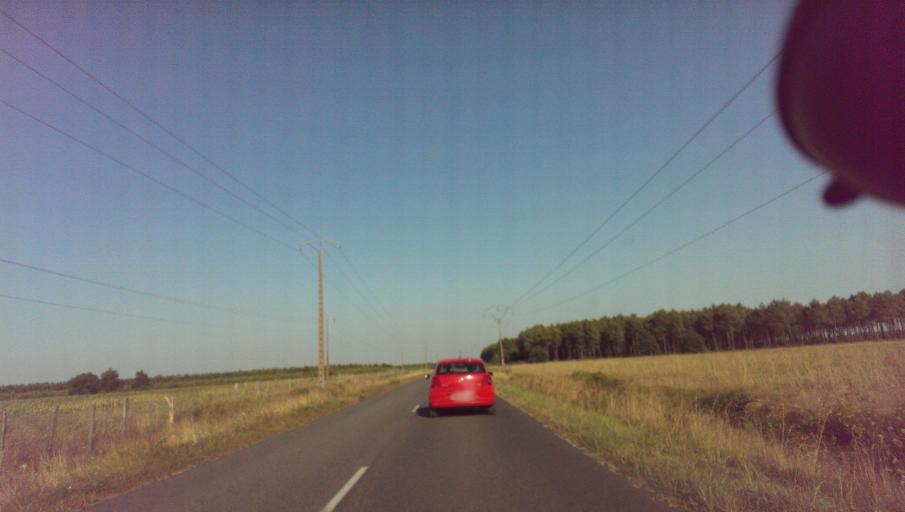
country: FR
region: Aquitaine
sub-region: Departement des Landes
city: Mimizan
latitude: 44.1861
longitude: -1.1999
